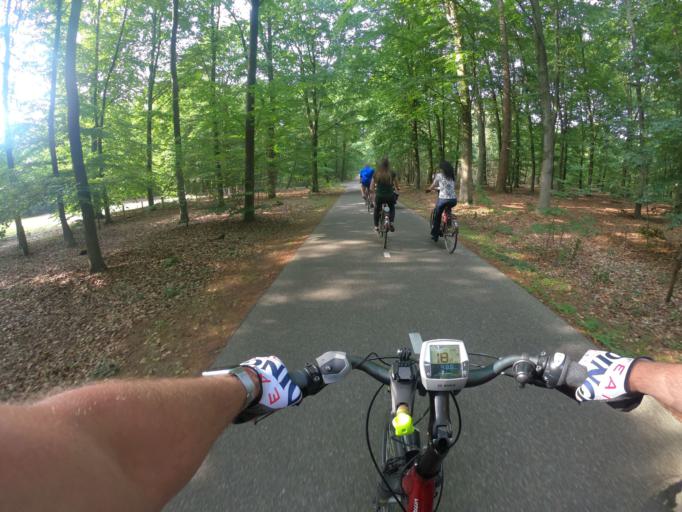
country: NL
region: Gelderland
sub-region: Gemeente Nijmegen
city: Nijmegen
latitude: 51.8024
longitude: 5.8587
